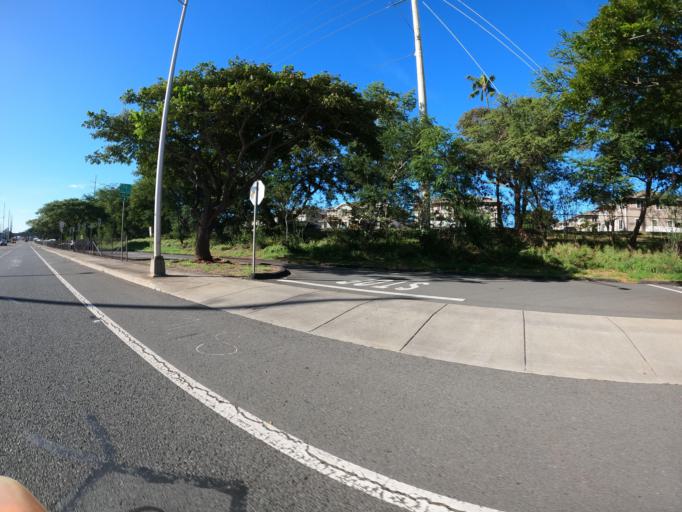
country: US
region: Hawaii
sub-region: Honolulu County
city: Halawa Heights
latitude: 21.3397
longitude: -157.9015
